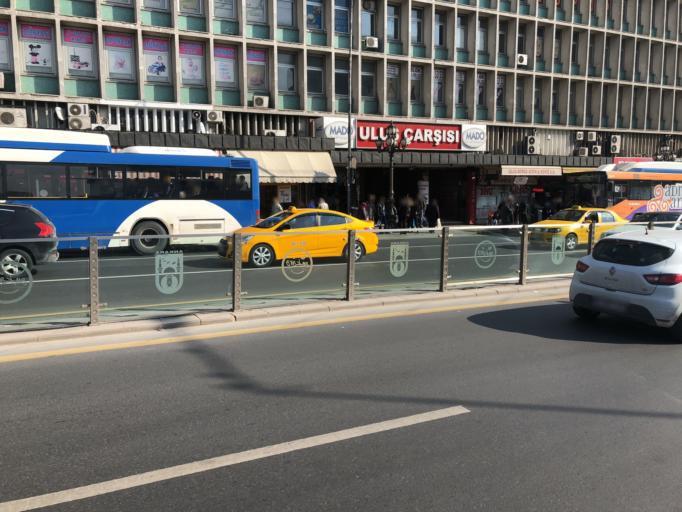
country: TR
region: Ankara
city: Ankara
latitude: 39.9414
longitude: 32.8543
